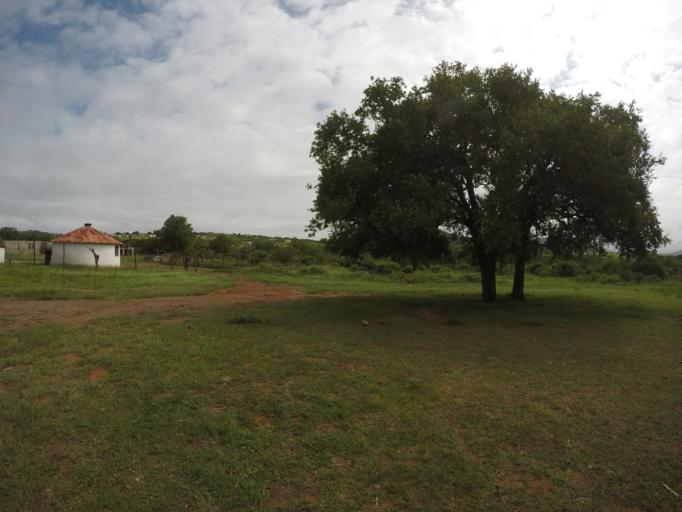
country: ZA
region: KwaZulu-Natal
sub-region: uThungulu District Municipality
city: Empangeni
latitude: -28.6147
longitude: 31.8510
